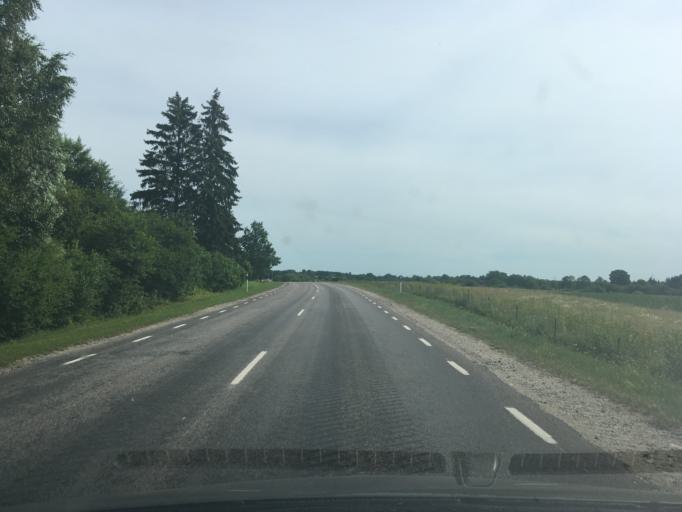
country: EE
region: Harju
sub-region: Nissi vald
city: Turba
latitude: 58.9091
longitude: 24.1420
